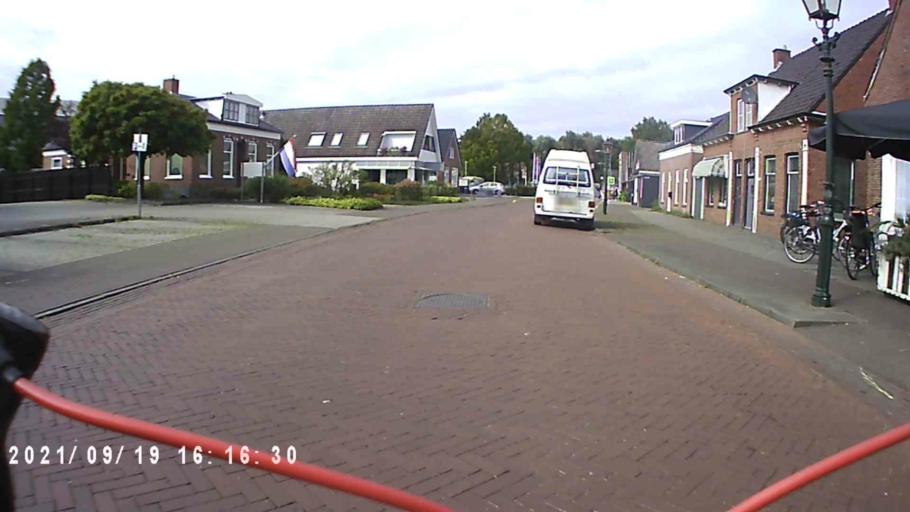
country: DE
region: Lower Saxony
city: Bunde
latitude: 53.1819
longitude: 7.2064
